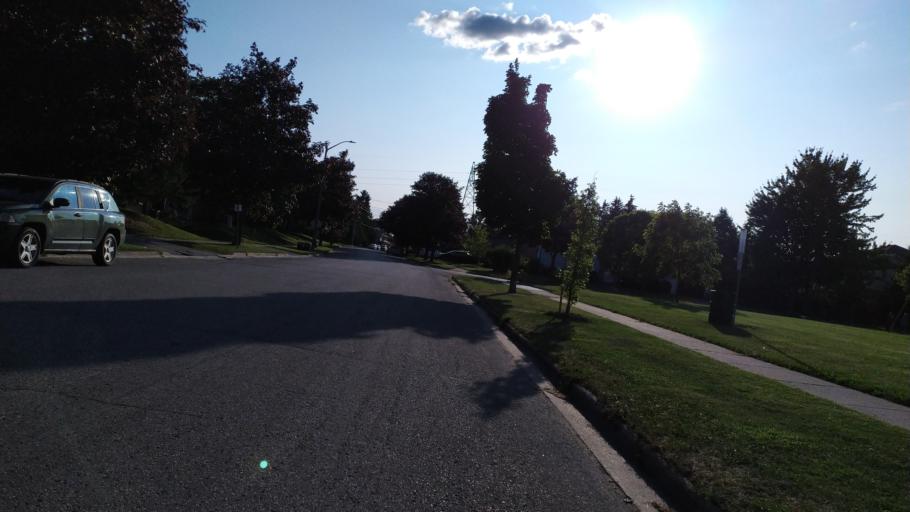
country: CA
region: Ontario
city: Stratford
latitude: 43.3729
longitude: -80.9536
